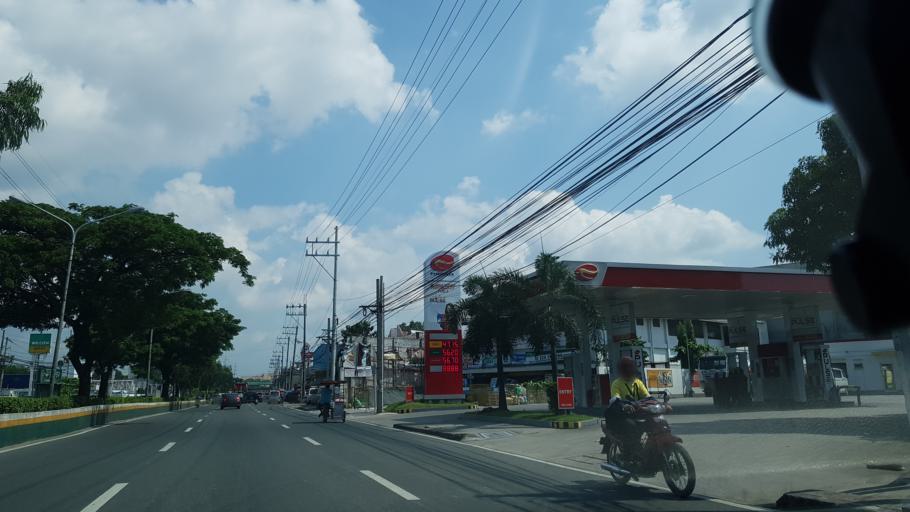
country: PH
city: Sambayanihan People's Village
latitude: 14.4819
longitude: 120.9961
